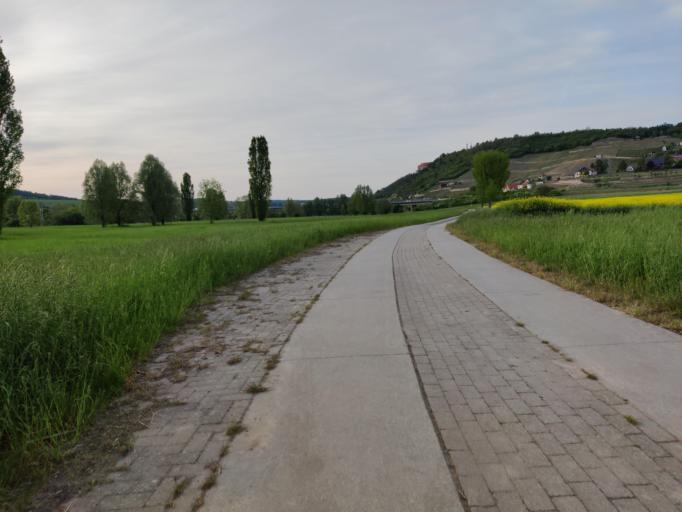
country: DE
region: Saxony-Anhalt
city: Freyburg
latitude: 51.1975
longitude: 11.7769
